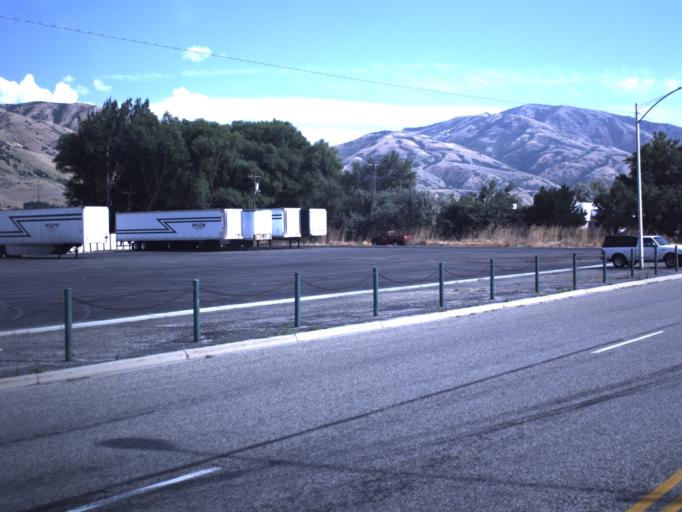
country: US
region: Utah
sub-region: Box Elder County
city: Brigham City
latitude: 41.5312
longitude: -112.0155
